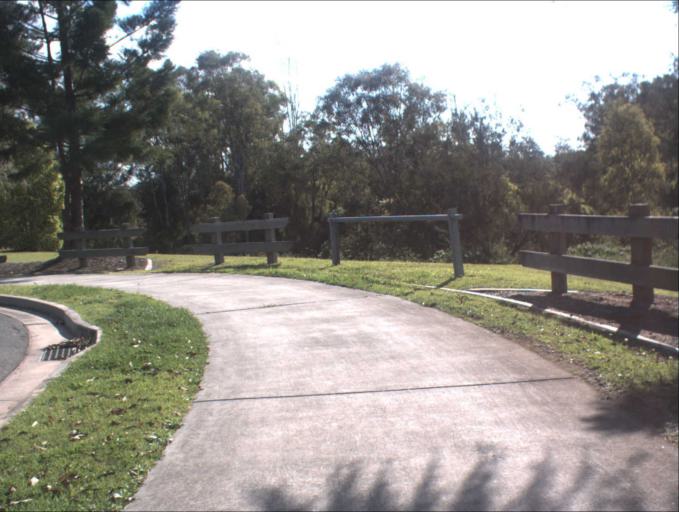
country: AU
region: Queensland
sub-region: Logan
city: Chambers Flat
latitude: -27.7717
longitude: 153.1010
